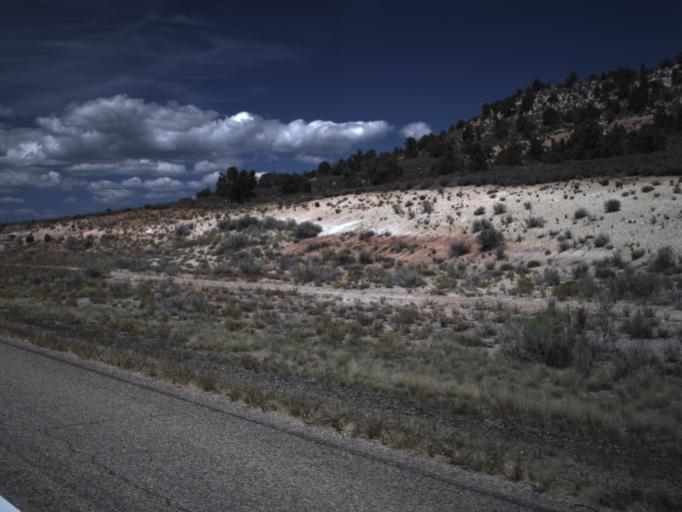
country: US
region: Utah
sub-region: Washington County
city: Ivins
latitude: 37.2743
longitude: -113.6459
